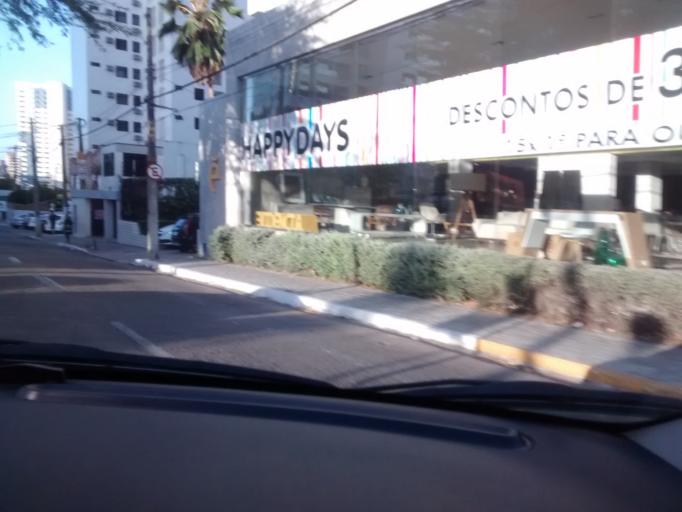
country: BR
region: Ceara
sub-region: Fortaleza
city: Fortaleza
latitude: -3.7398
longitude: -38.4941
